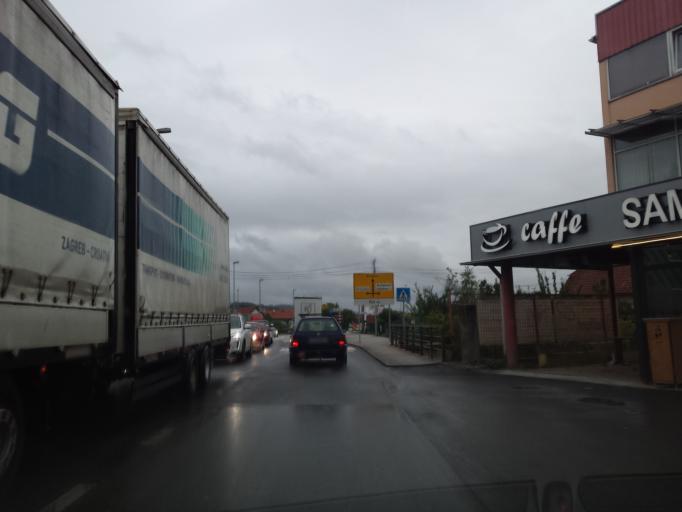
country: HR
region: Zagrebacka
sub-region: Grad Samobor
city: Samobor
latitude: 45.8061
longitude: 15.7179
